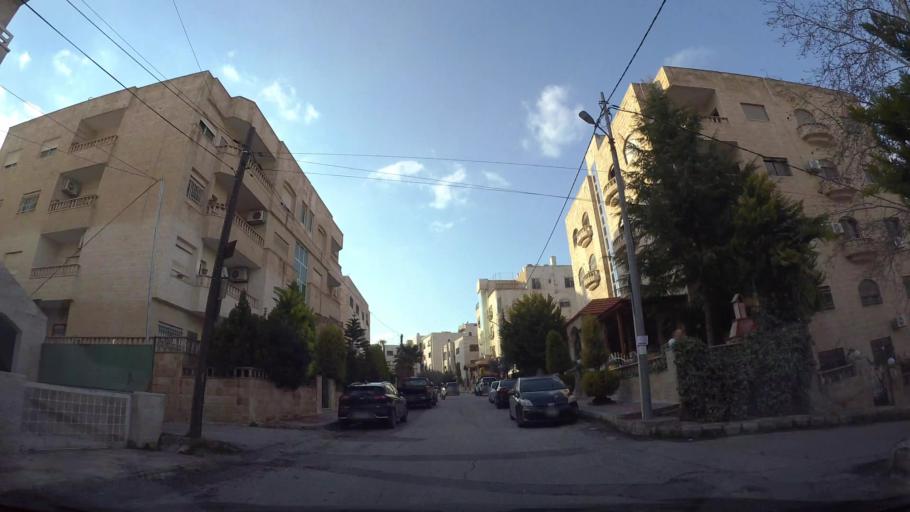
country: JO
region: Amman
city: Al Jubayhah
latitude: 31.9806
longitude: 35.8895
